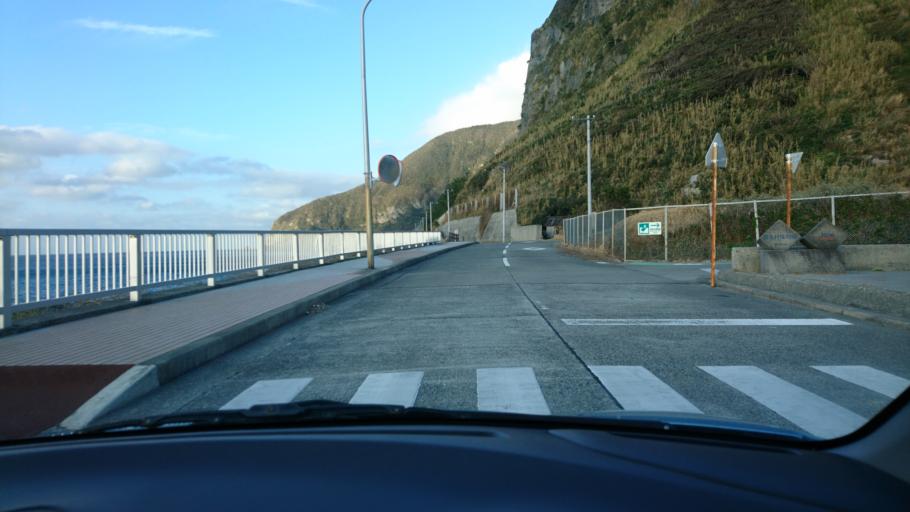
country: JP
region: Shizuoka
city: Shimoda
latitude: 34.3826
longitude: 139.2555
